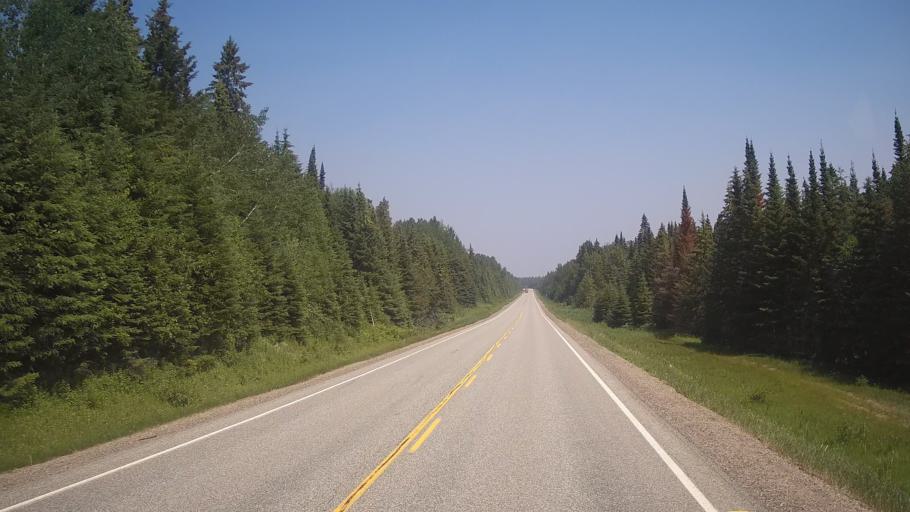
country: CA
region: Ontario
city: Timmins
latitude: 48.2051
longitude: -81.5772
